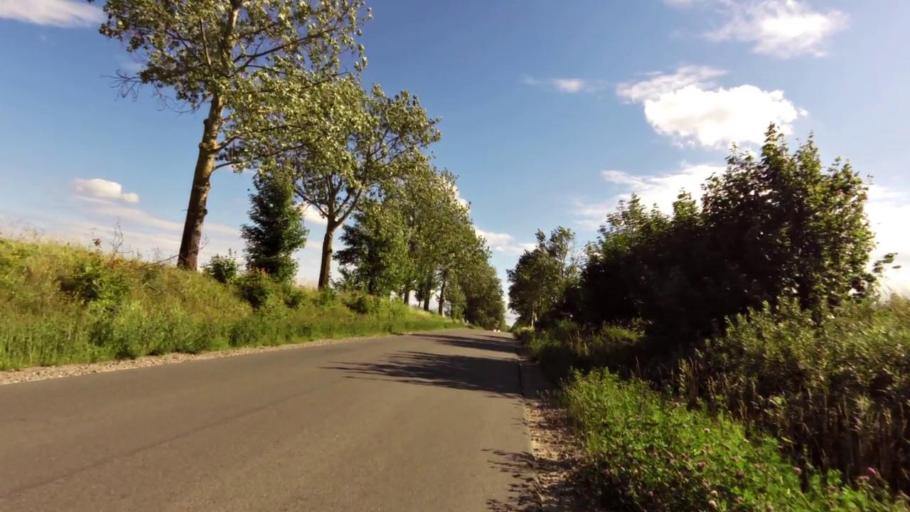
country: PL
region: West Pomeranian Voivodeship
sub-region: Powiat slawienski
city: Slawno
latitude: 54.4437
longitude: 16.7350
